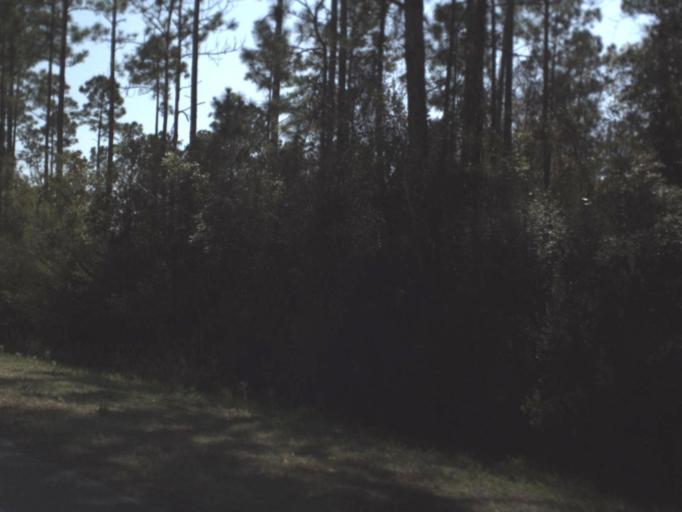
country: US
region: Florida
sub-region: Gulf County
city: Port Saint Joe
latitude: 29.7594
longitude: -85.2580
